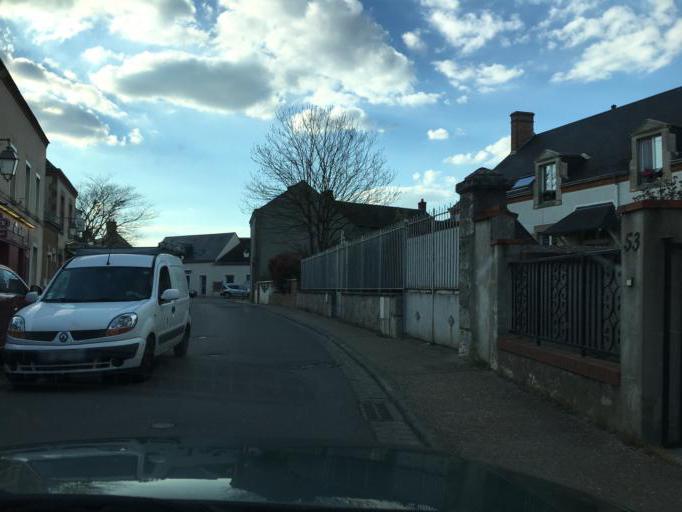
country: FR
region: Centre
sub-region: Departement du Loiret
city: Saint-Denis-en-Val
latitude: 47.8786
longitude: 1.9572
